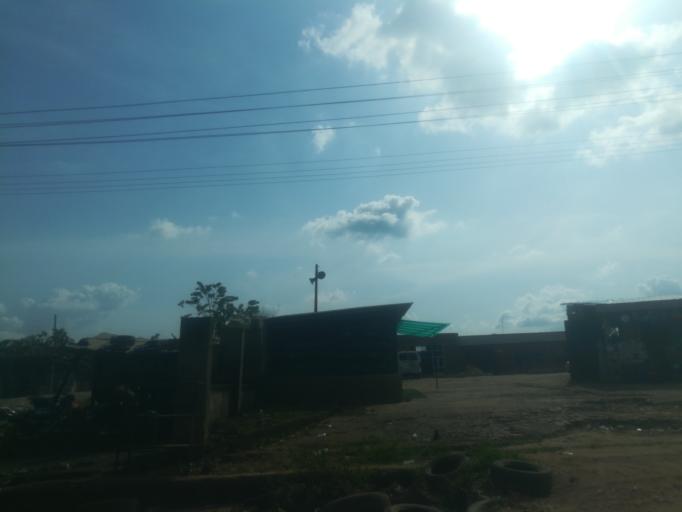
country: NG
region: Oyo
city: Ido
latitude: 7.3953
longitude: 3.8103
